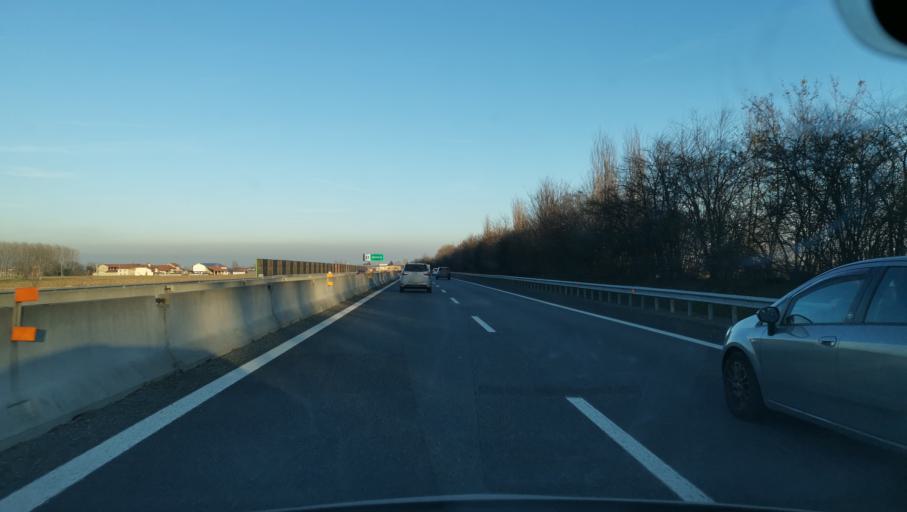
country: IT
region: Piedmont
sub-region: Provincia di Torino
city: Piscina
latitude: 44.8999
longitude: 7.4162
